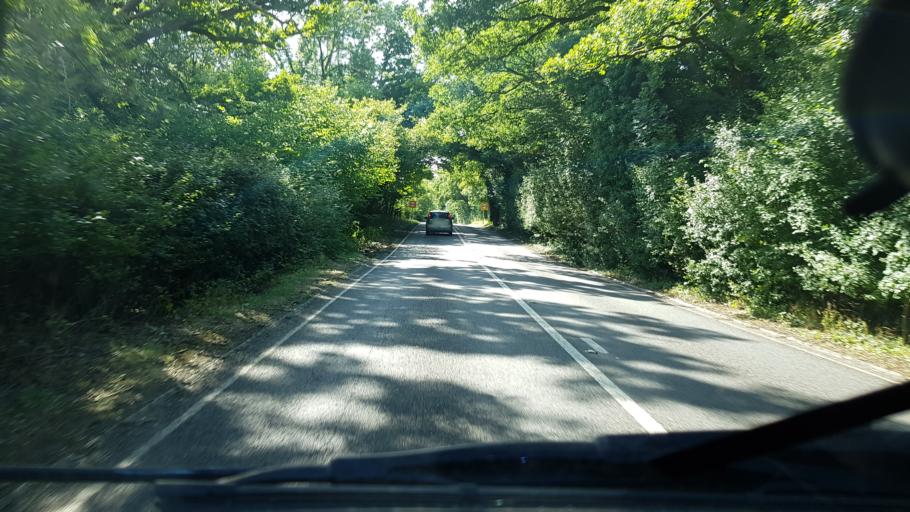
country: GB
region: England
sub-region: West Sussex
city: Rudgwick
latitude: 51.0859
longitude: -0.4435
